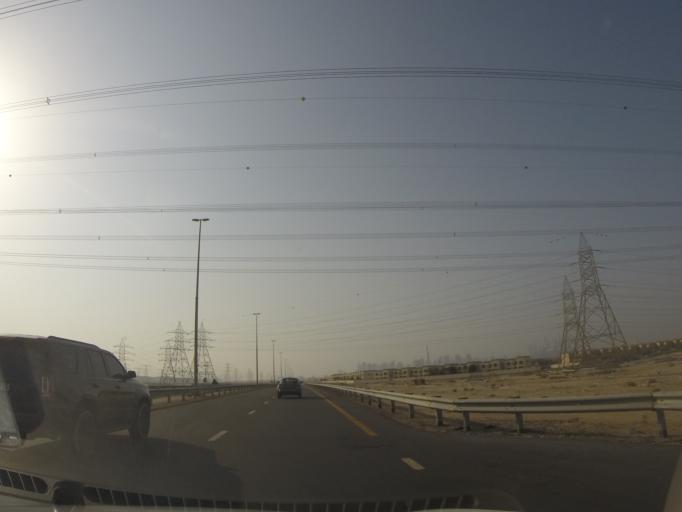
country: AE
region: Dubai
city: Dubai
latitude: 25.0365
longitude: 55.1617
